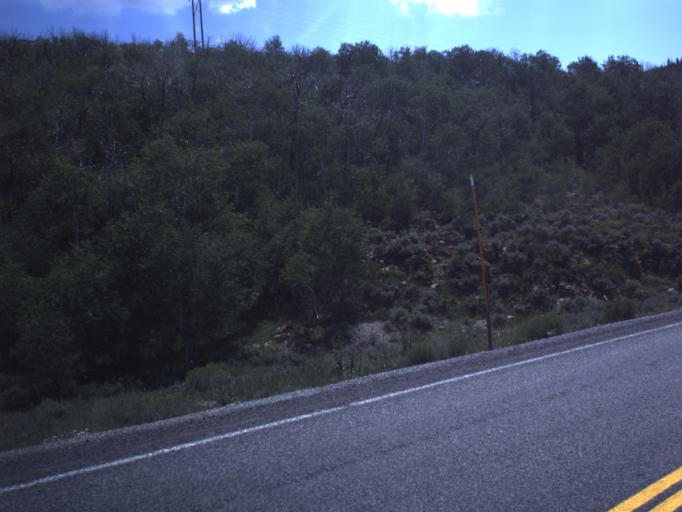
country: US
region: Utah
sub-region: Carbon County
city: Helper
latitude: 39.8224
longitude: -111.1351
